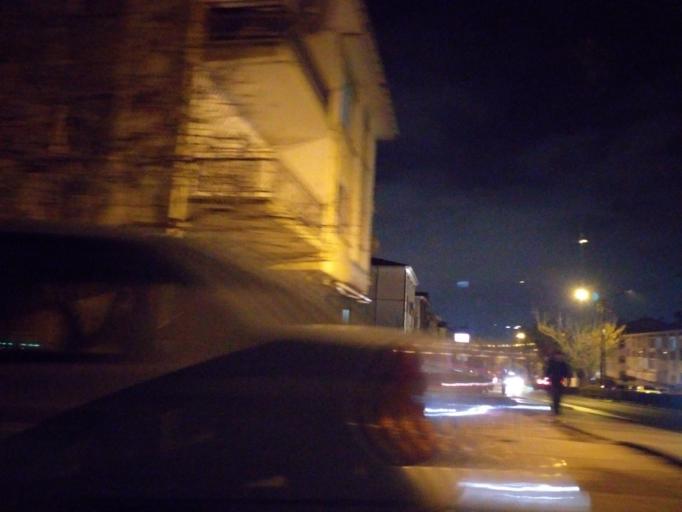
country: TR
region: Ankara
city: Ankara
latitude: 39.9778
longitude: 32.8245
